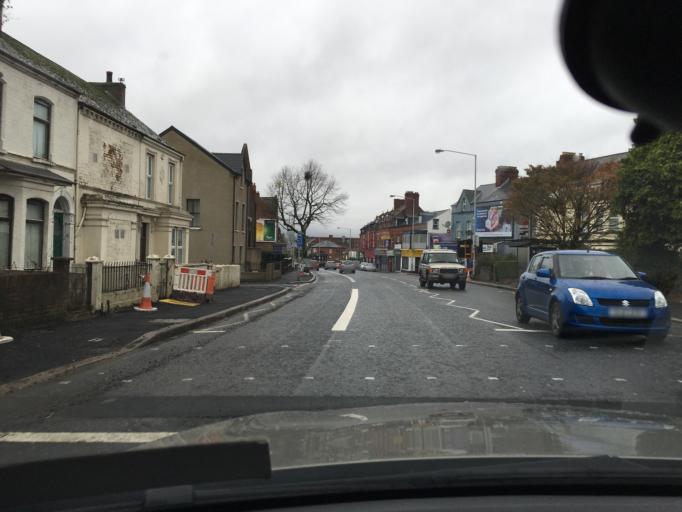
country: GB
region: Northern Ireland
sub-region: Castlereagh District
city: Castlereagh
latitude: 54.5971
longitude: -5.8849
